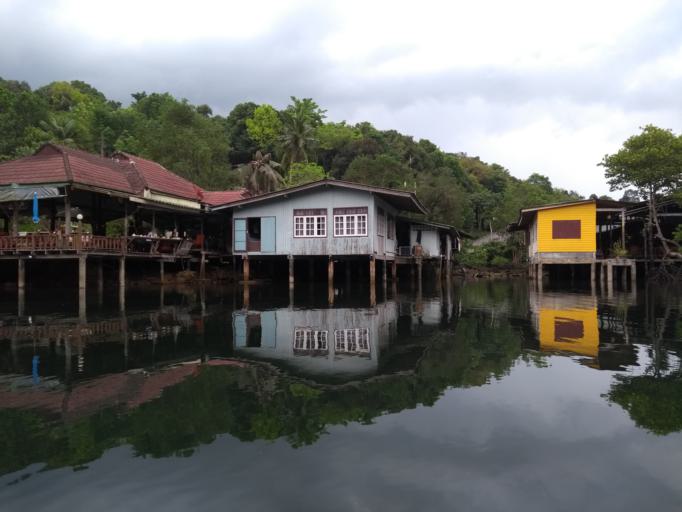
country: TH
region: Trat
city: Ko Kut
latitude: 11.6343
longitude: 102.5490
